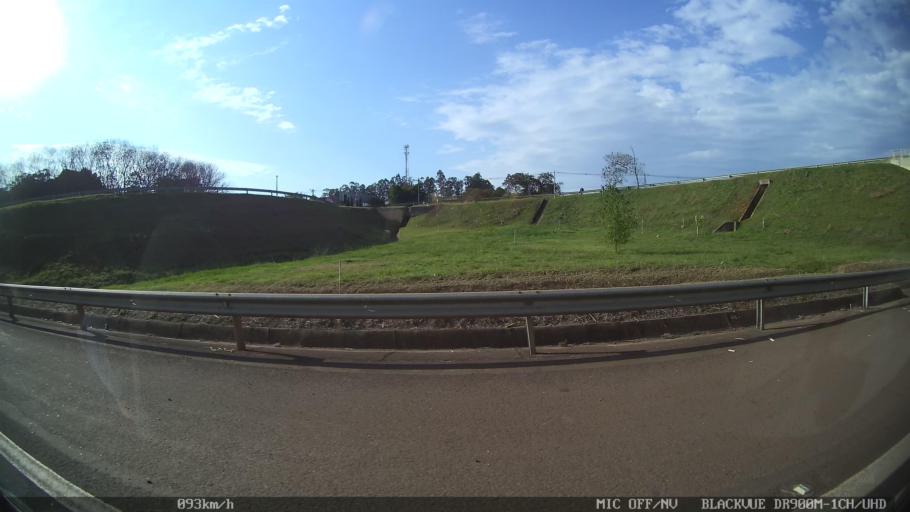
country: BR
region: Sao Paulo
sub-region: Cosmopolis
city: Cosmopolis
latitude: -22.6552
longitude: -47.1816
